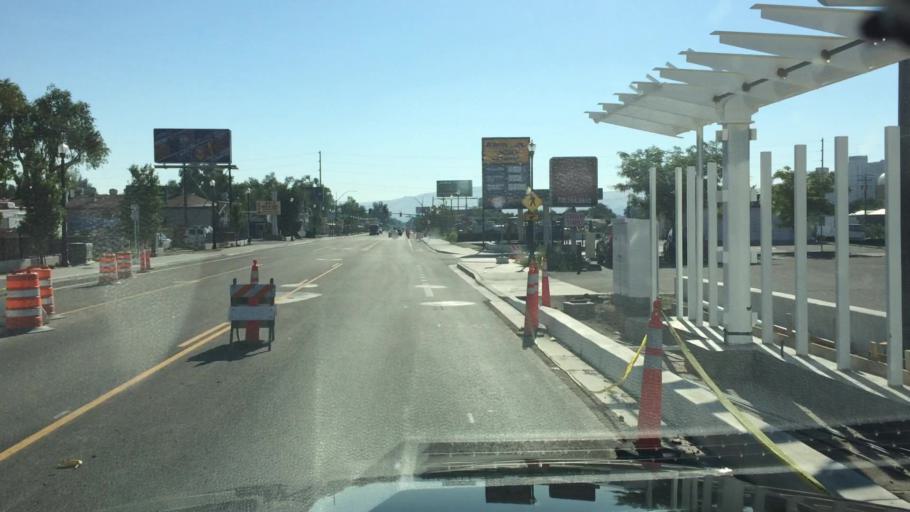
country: US
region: Nevada
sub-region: Washoe County
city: Sparks
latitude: 39.5362
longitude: -119.7740
